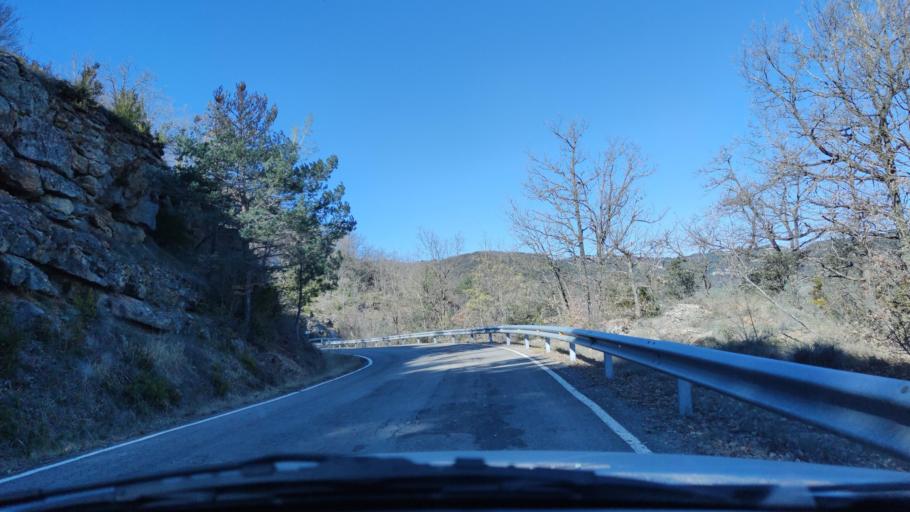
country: ES
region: Catalonia
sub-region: Provincia de Lleida
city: Llimiana
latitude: 42.0429
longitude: 1.0554
